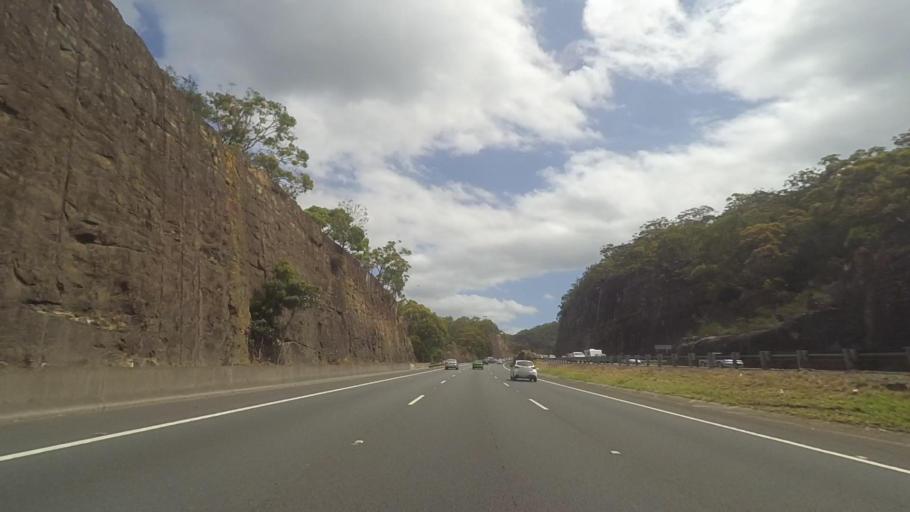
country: AU
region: New South Wales
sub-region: Hornsby Shire
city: Berowra
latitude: -33.5455
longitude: 151.1970
